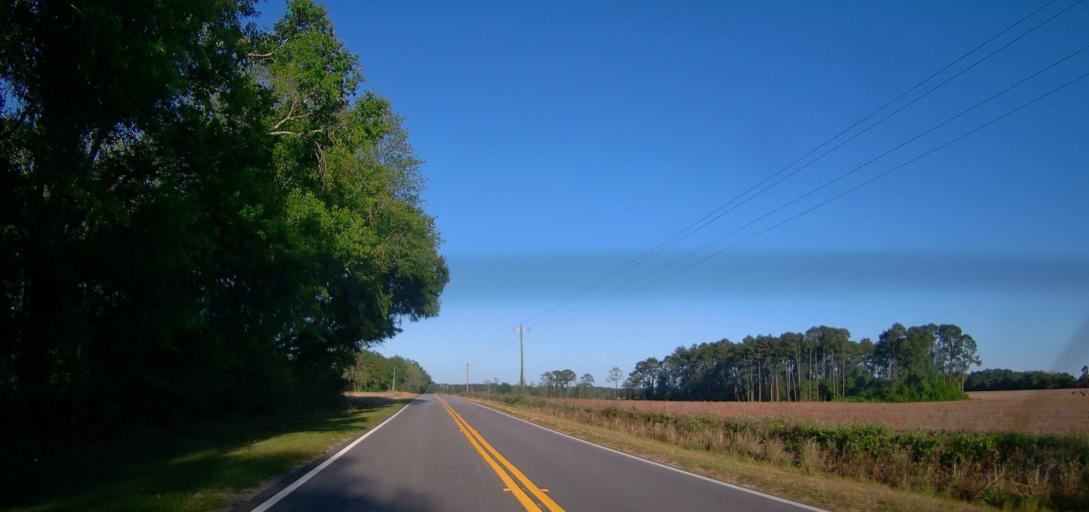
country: US
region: Georgia
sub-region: Ben Hill County
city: Fitzgerald
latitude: 31.6566
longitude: -83.1726
